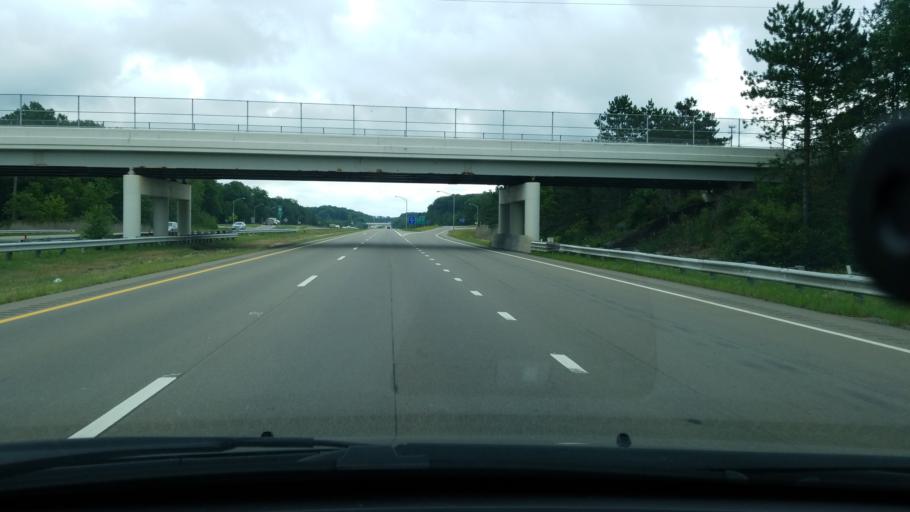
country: US
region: Ohio
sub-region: Lorain County
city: Vermilion
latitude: 41.4023
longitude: -82.3419
